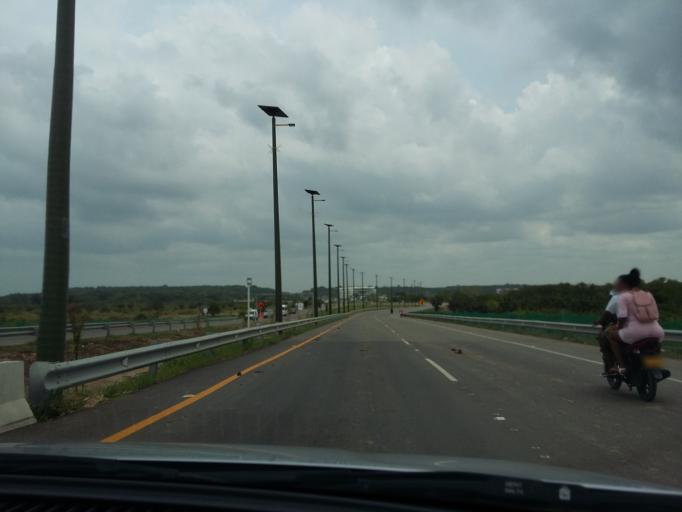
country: CO
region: Bolivar
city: Cartagena
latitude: 10.4988
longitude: -75.4775
